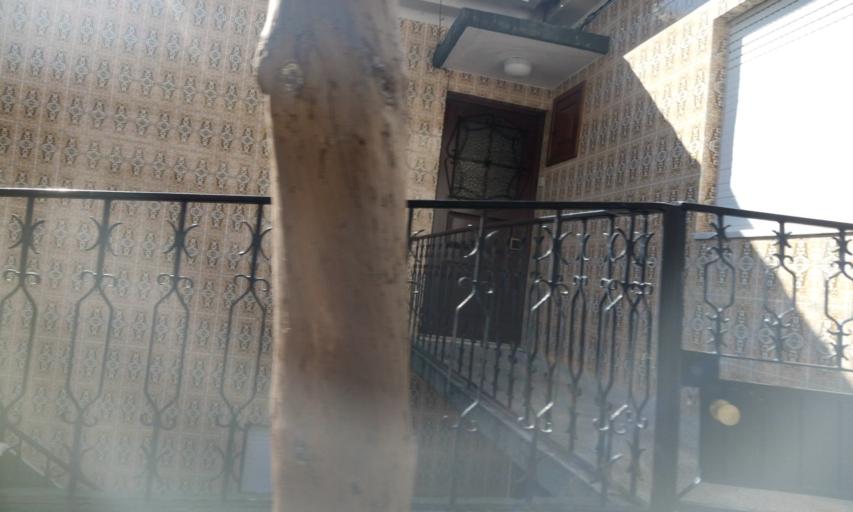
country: PT
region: Guarda
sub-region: Manteigas
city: Manteigas
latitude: 40.4714
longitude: -7.6004
